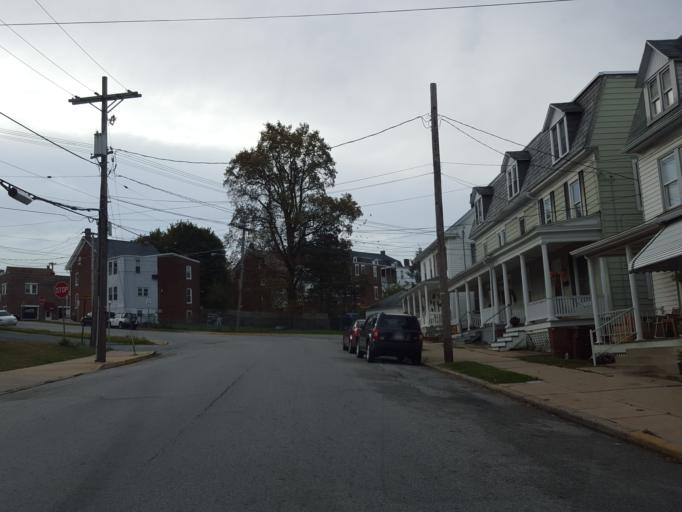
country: US
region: Pennsylvania
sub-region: York County
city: Red Lion
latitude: 39.8988
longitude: -76.6120
